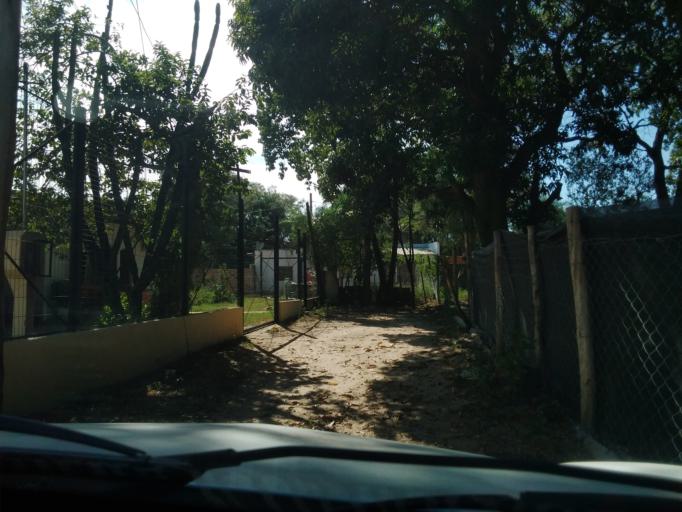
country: AR
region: Corrientes
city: Corrientes
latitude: -27.5103
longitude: -58.8074
